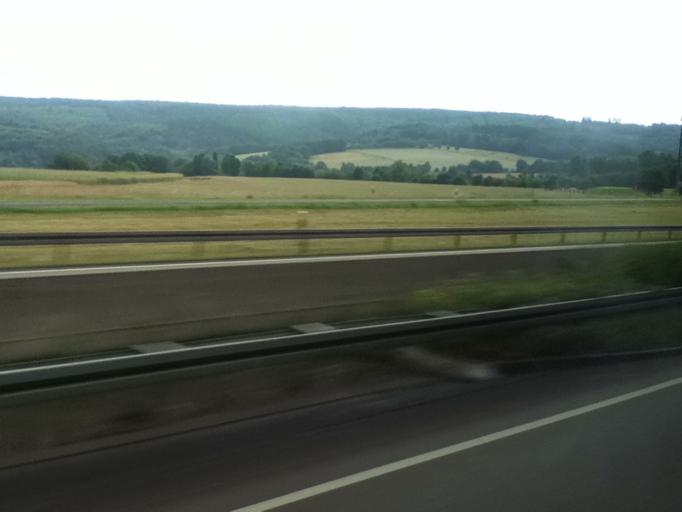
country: DE
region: Thuringia
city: Grossensee
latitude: 50.9437
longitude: 9.9371
